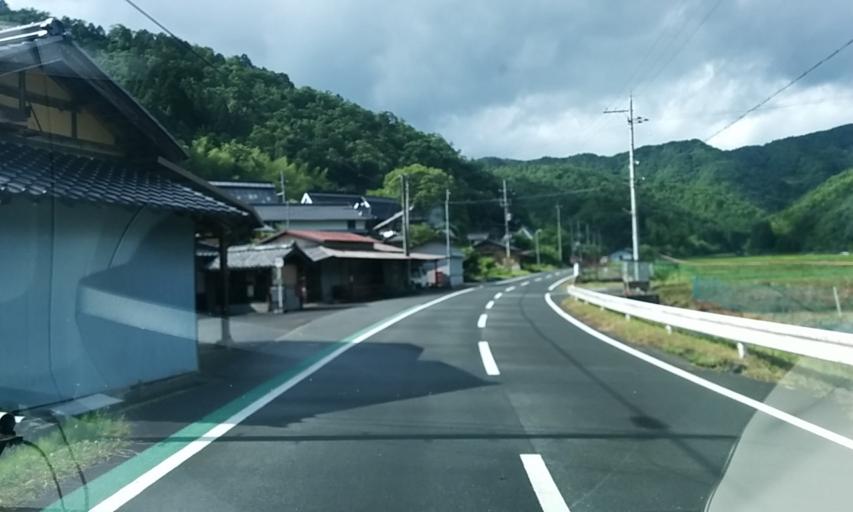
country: JP
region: Kyoto
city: Ayabe
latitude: 35.3856
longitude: 135.2571
